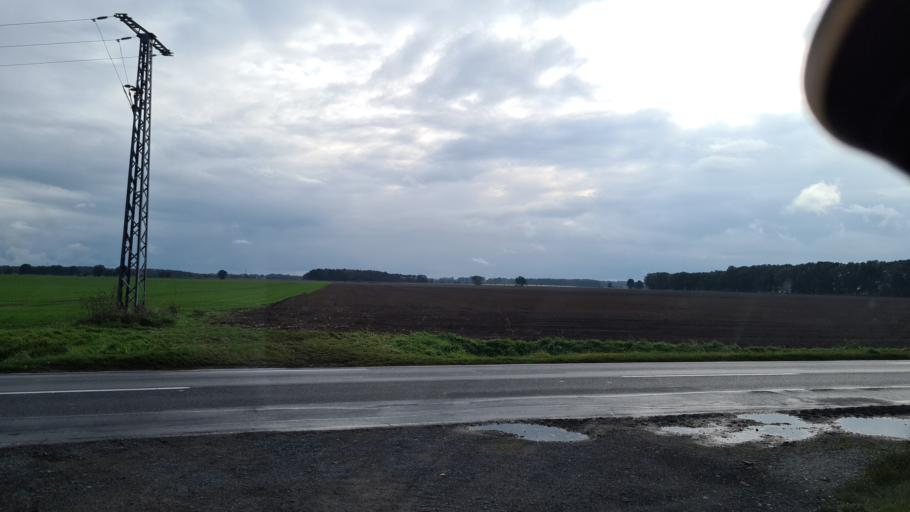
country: DE
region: Brandenburg
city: Schonewalde
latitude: 51.6897
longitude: 13.6233
